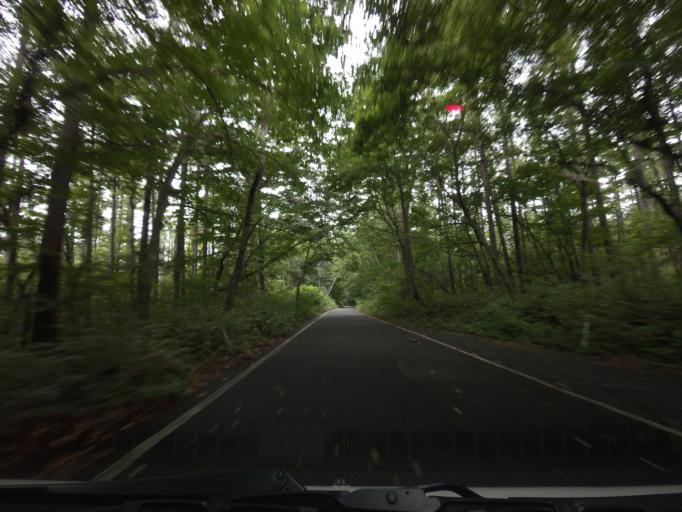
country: JP
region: Fukushima
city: Motomiya
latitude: 37.5761
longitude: 140.3244
